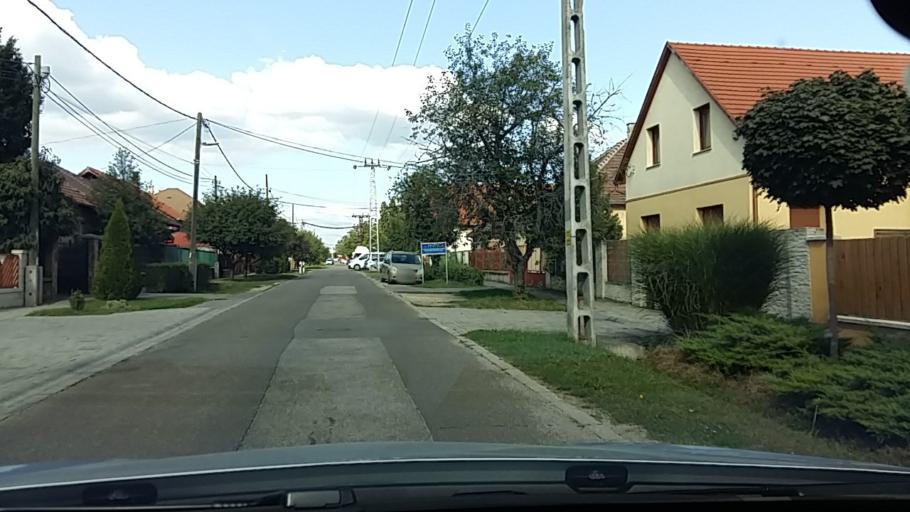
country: HU
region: Pest
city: Vecses
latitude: 47.4107
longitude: 19.2629
